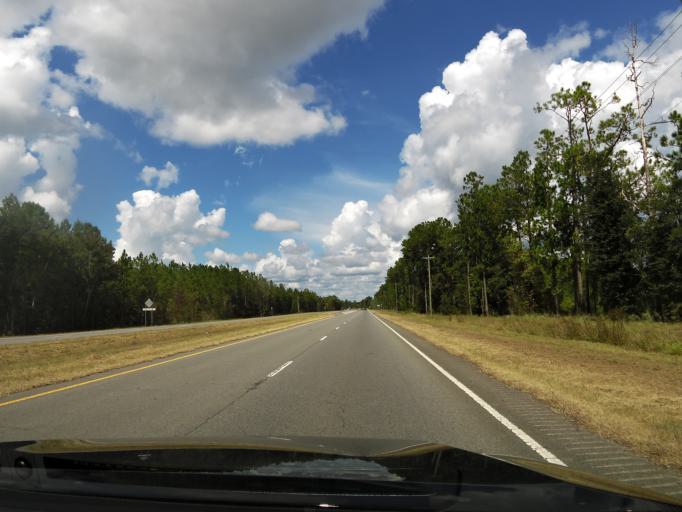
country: US
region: Georgia
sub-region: Charlton County
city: Folkston
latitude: 30.7893
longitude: -81.9822
